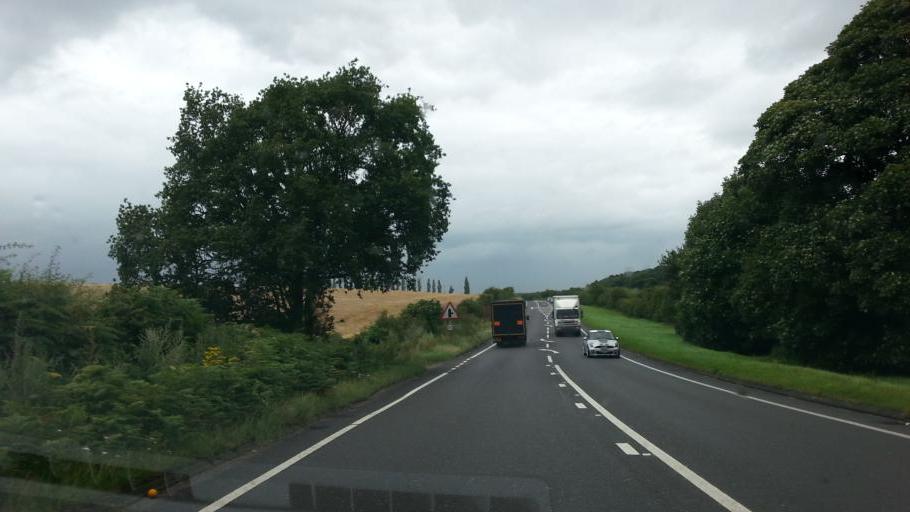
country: GB
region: England
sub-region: Nottinghamshire
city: Bilsthorpe
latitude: 53.1239
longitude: -1.0592
